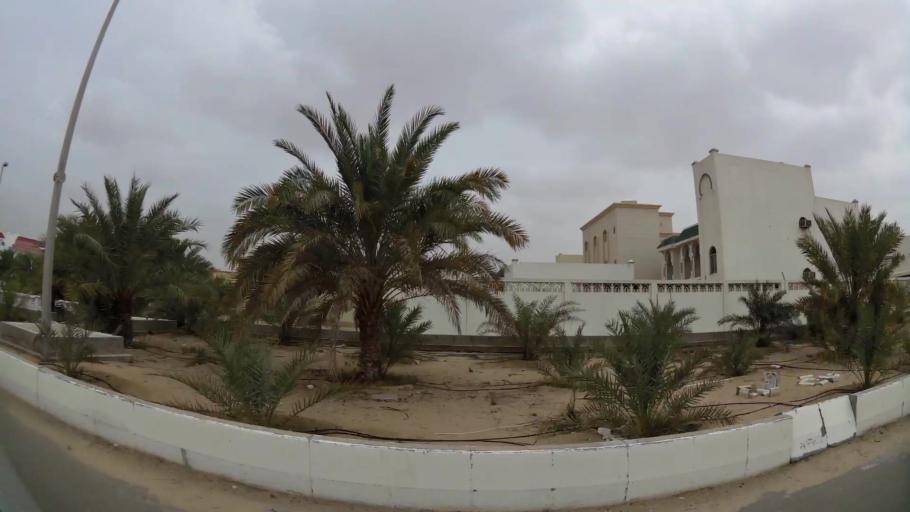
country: AE
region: Abu Dhabi
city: Abu Dhabi
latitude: 24.3758
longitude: 54.6618
